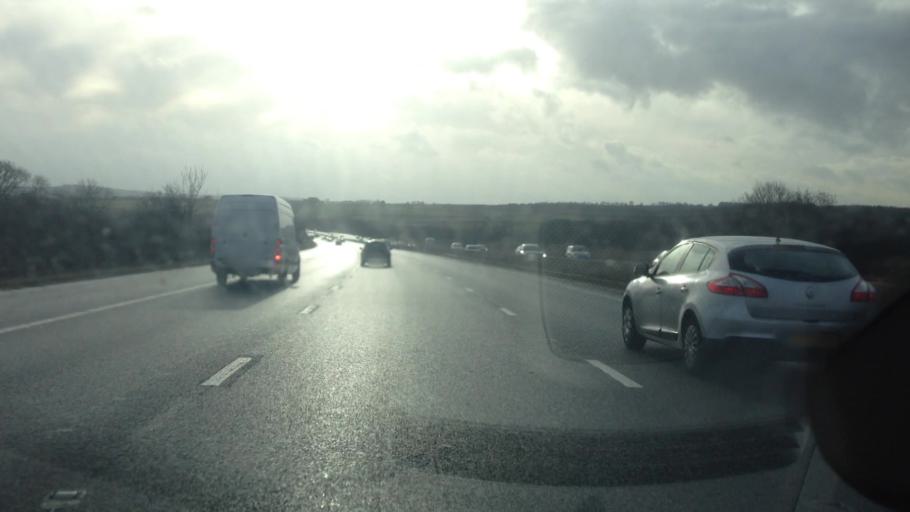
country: GB
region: England
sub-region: Barnsley
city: Darton
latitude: 53.6136
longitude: -1.5523
